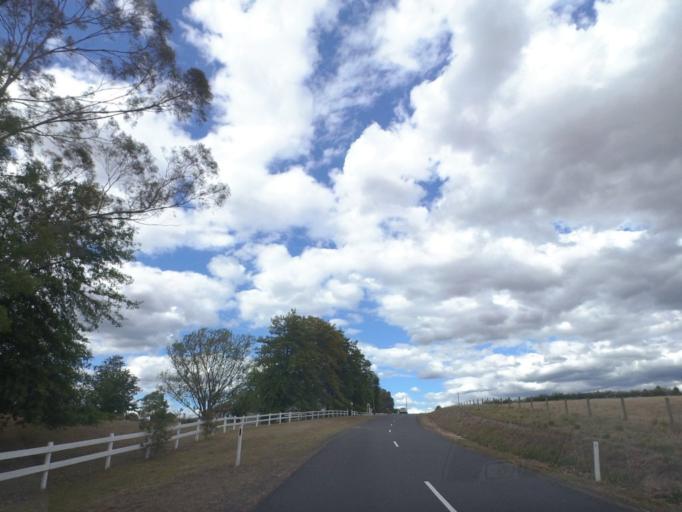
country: AU
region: Victoria
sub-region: Yarra Ranges
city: Yarra Glen
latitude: -37.6443
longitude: 145.4084
